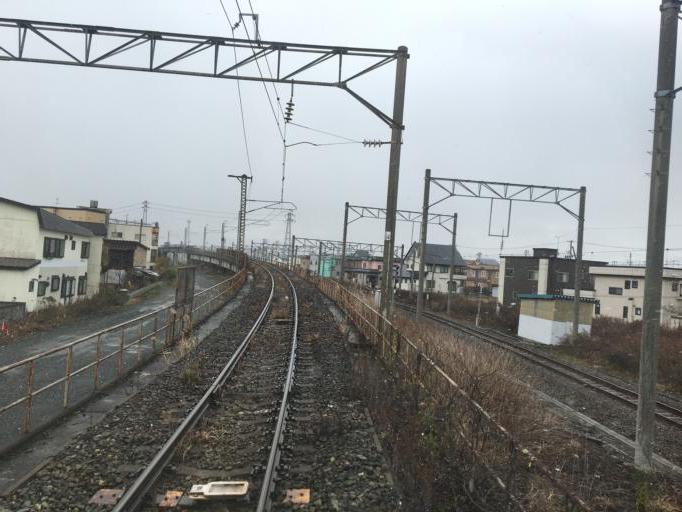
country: JP
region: Aomori
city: Aomori Shi
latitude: 40.8216
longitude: 140.7327
